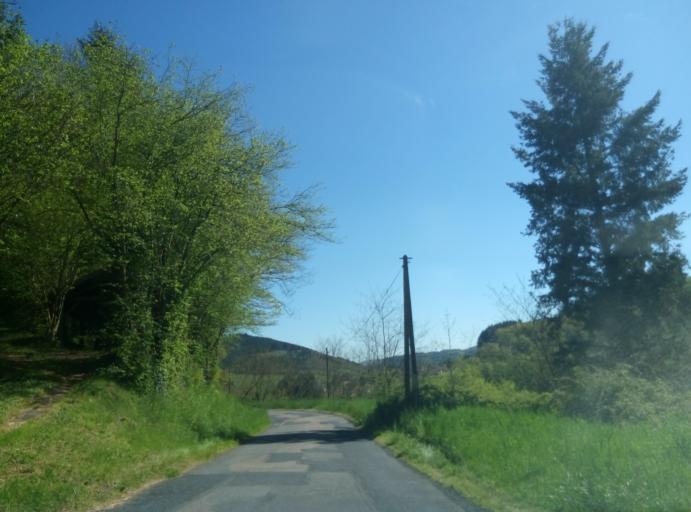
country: FR
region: Rhone-Alpes
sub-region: Departement du Rhone
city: Grandris
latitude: 46.0591
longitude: 4.4932
